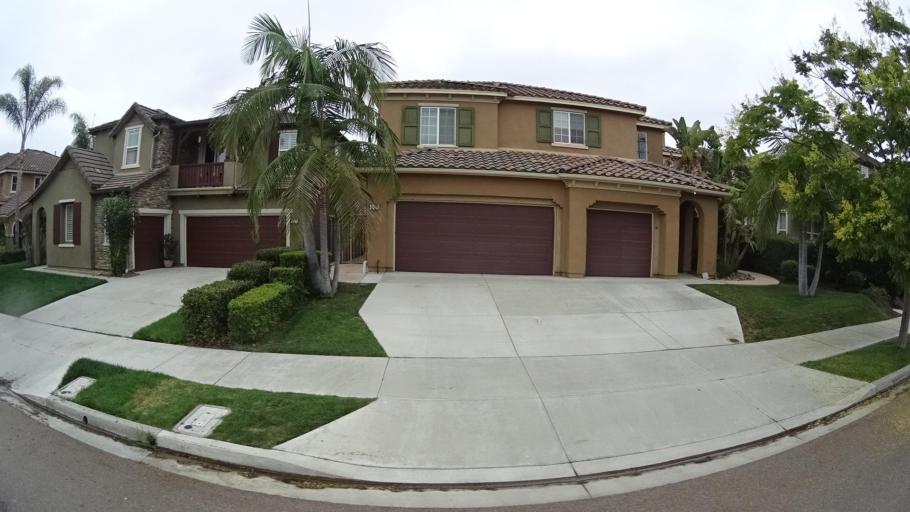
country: US
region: California
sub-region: San Diego County
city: Fairbanks Ranch
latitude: 33.0281
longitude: -117.1177
